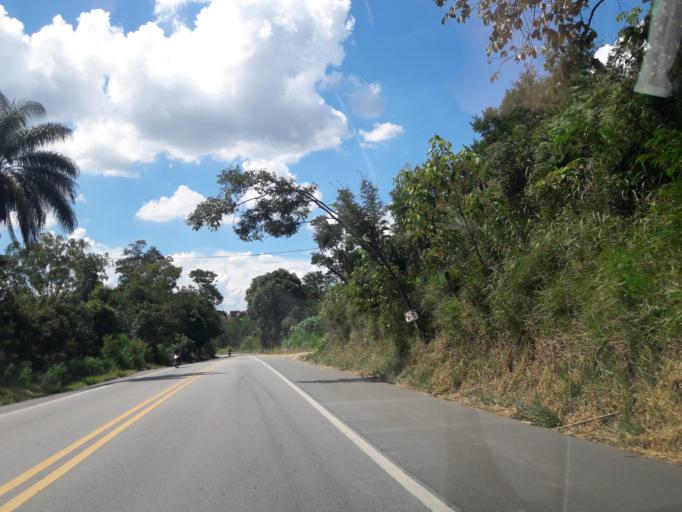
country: BR
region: Sao Paulo
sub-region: Campo Limpo Paulista
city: Campo Limpo Paulista
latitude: -23.2382
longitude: -46.7919
